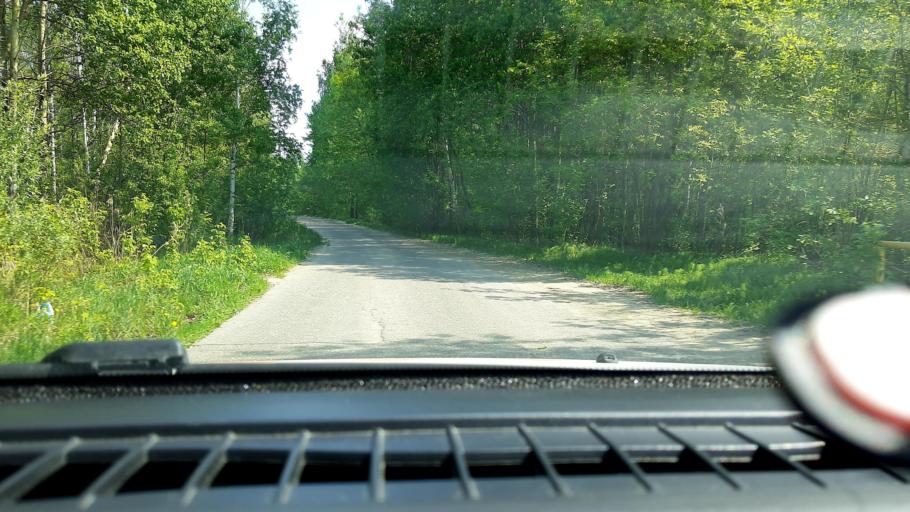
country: RU
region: Nizjnij Novgorod
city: Kstovo
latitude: 56.1472
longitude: 44.1254
